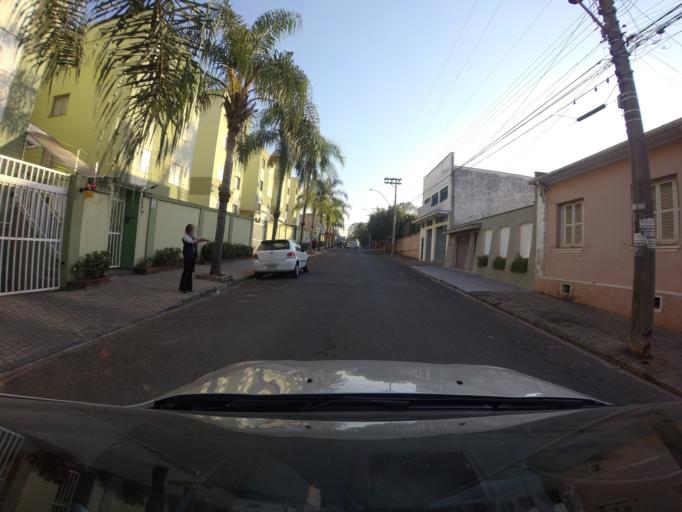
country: BR
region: Sao Paulo
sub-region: Piracicaba
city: Piracicaba
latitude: -22.7320
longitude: -47.6451
